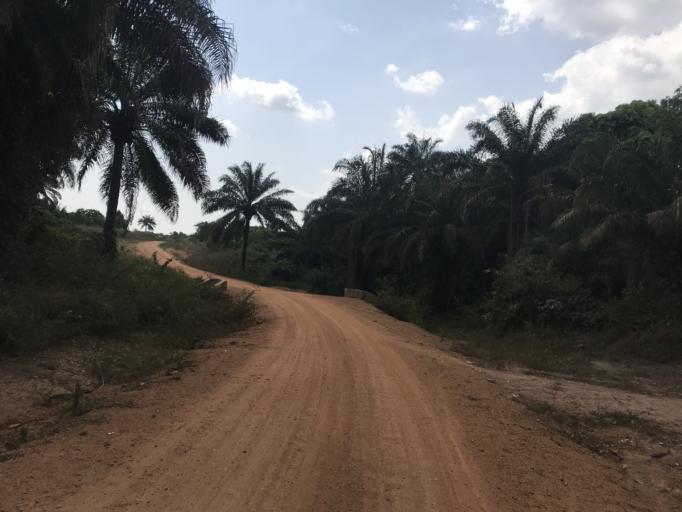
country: NG
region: Osun
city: Ifon
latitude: 7.9738
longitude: 4.5108
